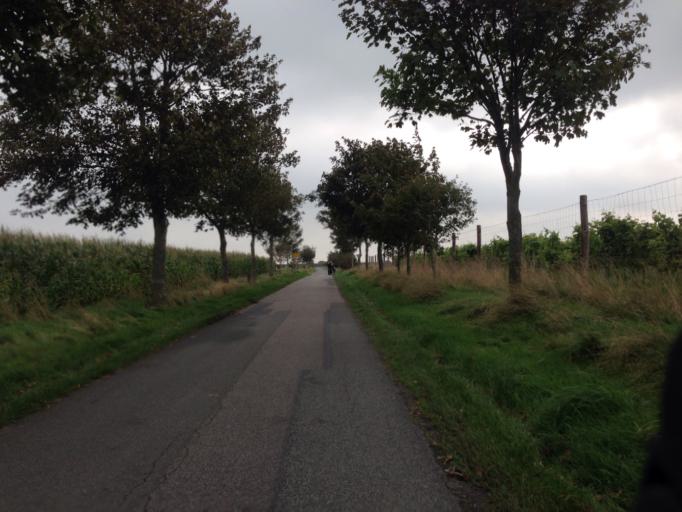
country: DE
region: Schleswig-Holstein
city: Alkersum
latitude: 54.7046
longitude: 8.5057
